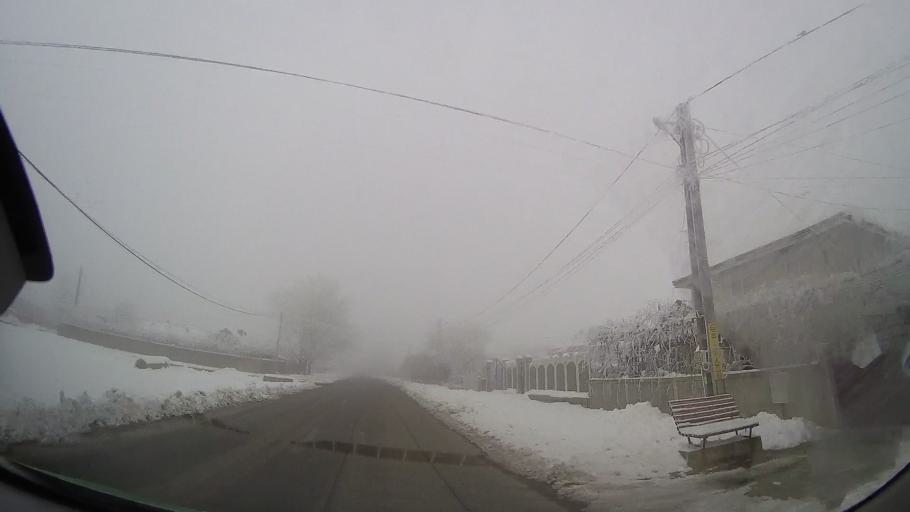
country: RO
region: Neamt
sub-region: Comuna Sabaoani
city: Sabaoani
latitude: 47.0212
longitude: 26.8643
